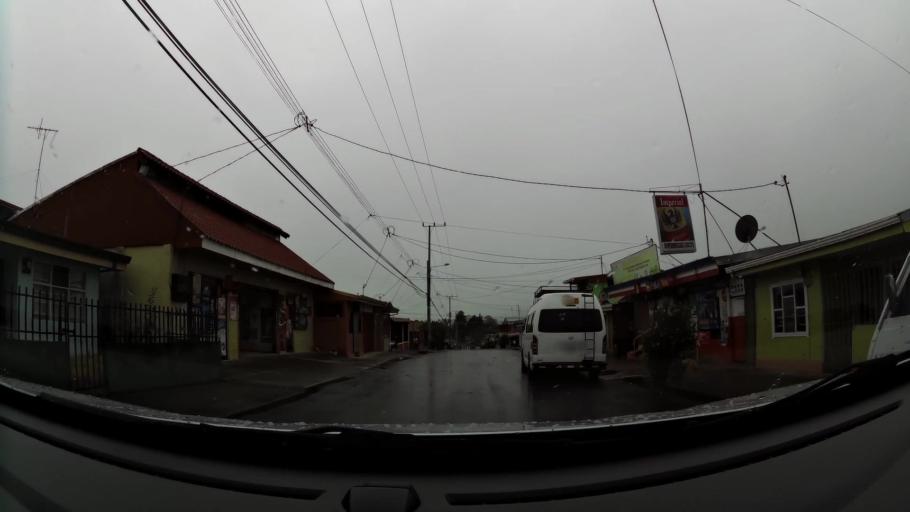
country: CR
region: Cartago
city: Paraiso
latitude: 9.8388
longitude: -83.8627
